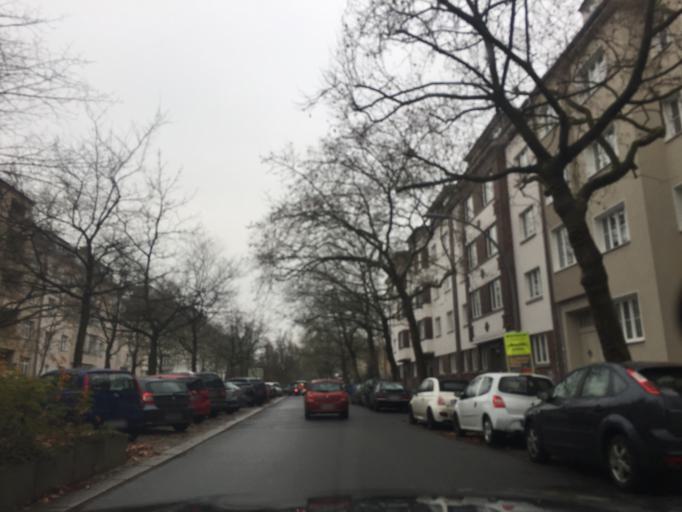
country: DE
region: Berlin
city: Westend
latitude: 52.5157
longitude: 13.2598
